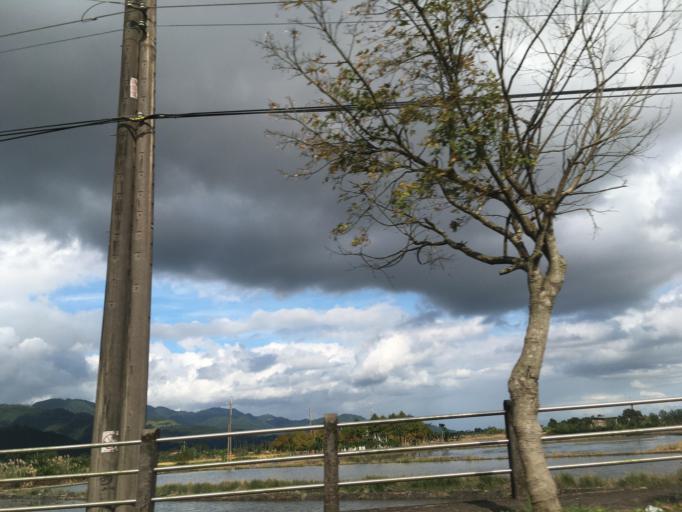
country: TW
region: Taiwan
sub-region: Yilan
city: Yilan
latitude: 24.6656
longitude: 121.6169
